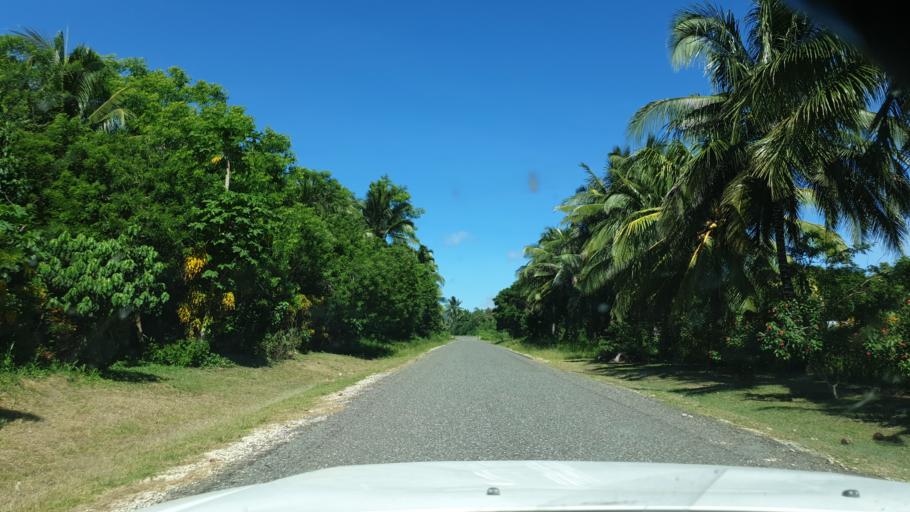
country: PG
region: Madang
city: Madang
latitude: -4.5440
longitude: 145.4956
